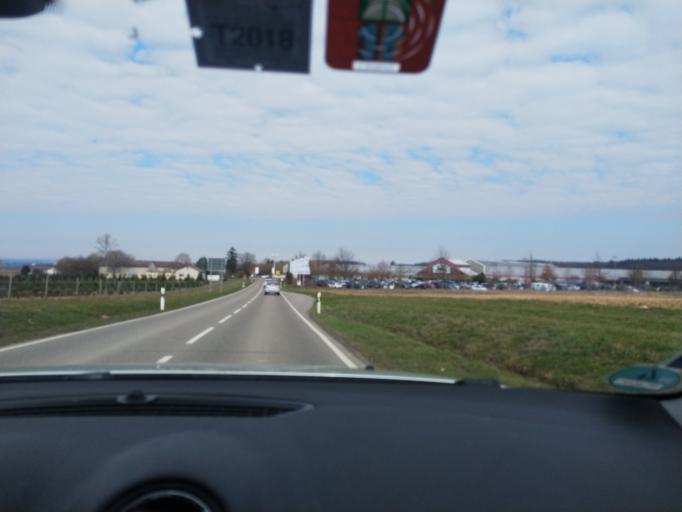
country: DE
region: Baden-Wuerttemberg
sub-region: Regierungsbezirk Stuttgart
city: Neckarwestheim
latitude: 49.0636
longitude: 9.1974
